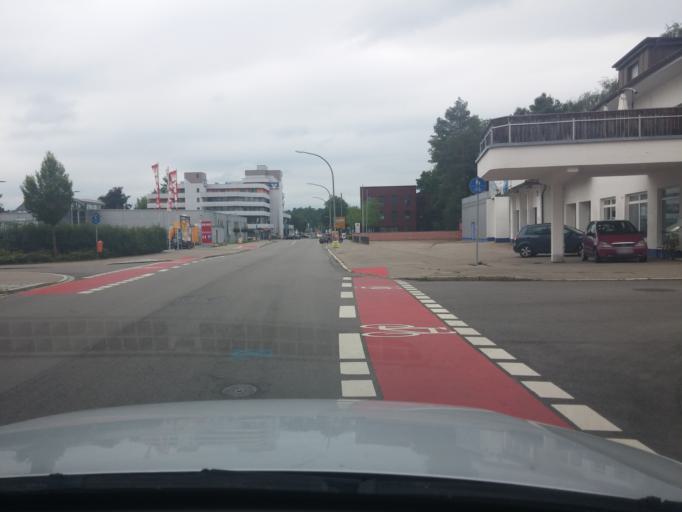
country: DE
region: Bavaria
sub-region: Swabia
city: Memmingen
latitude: 47.9809
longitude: 10.1754
